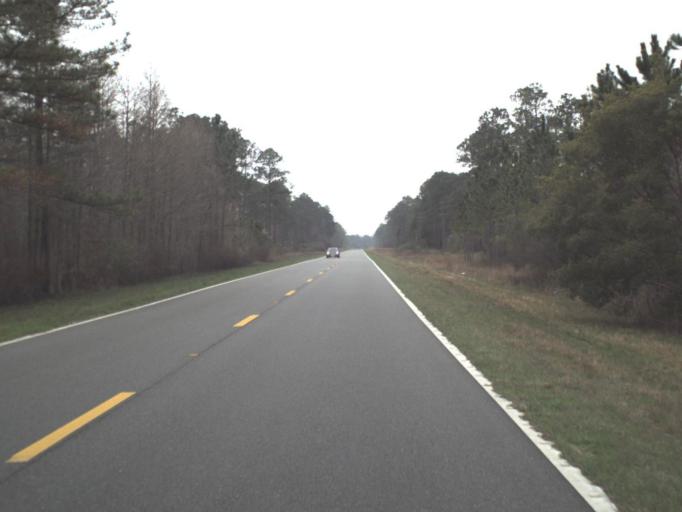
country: US
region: Florida
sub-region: Liberty County
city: Bristol
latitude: 30.2730
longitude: -84.8473
